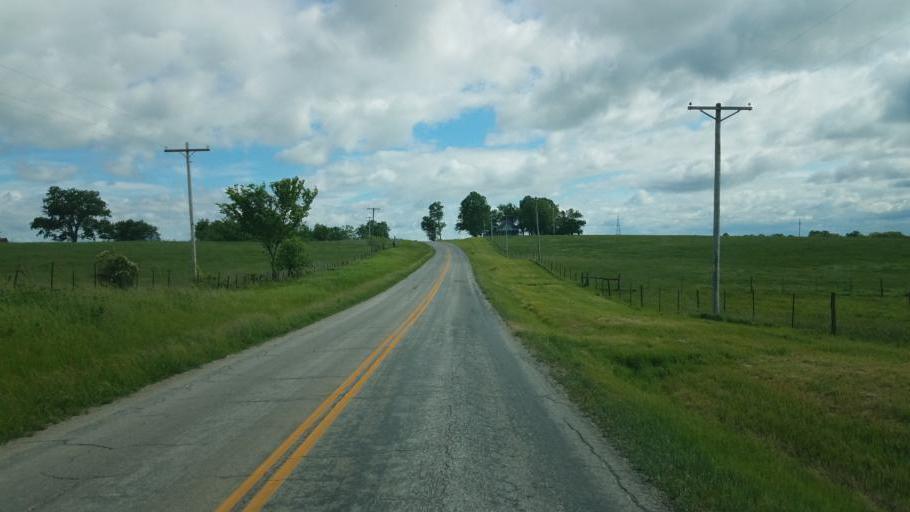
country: US
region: Missouri
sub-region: Mercer County
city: Princeton
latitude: 40.2957
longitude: -93.6806
